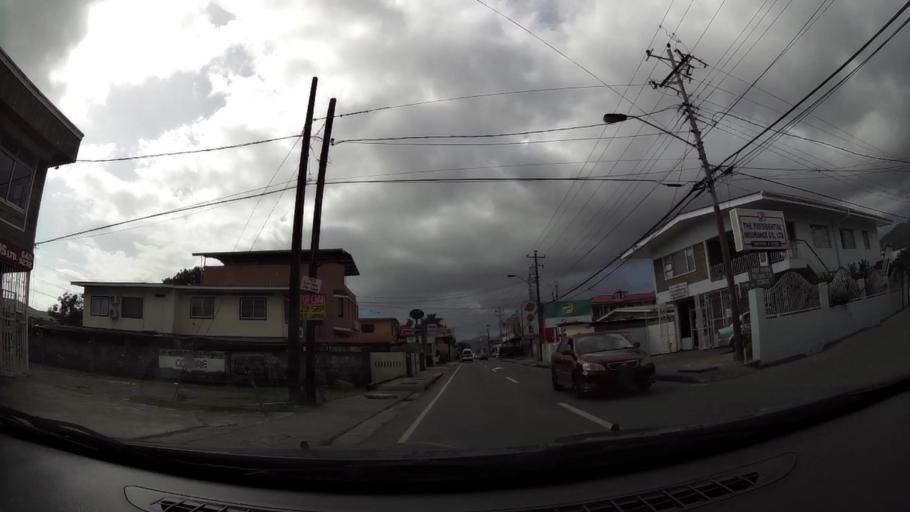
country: TT
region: Tunapuna/Piarco
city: Paradise
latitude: 10.6405
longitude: -61.3517
